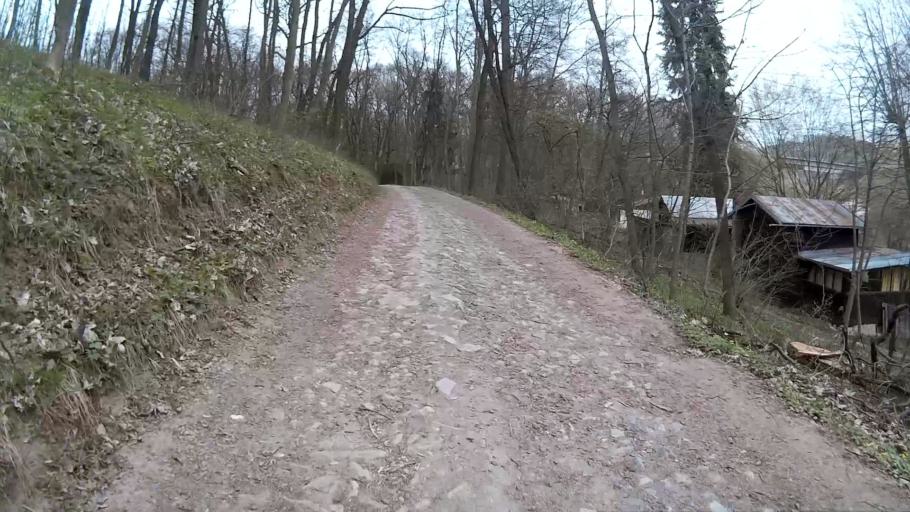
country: CZ
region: South Moravian
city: Ivancice
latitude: 49.0797
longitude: 16.4082
